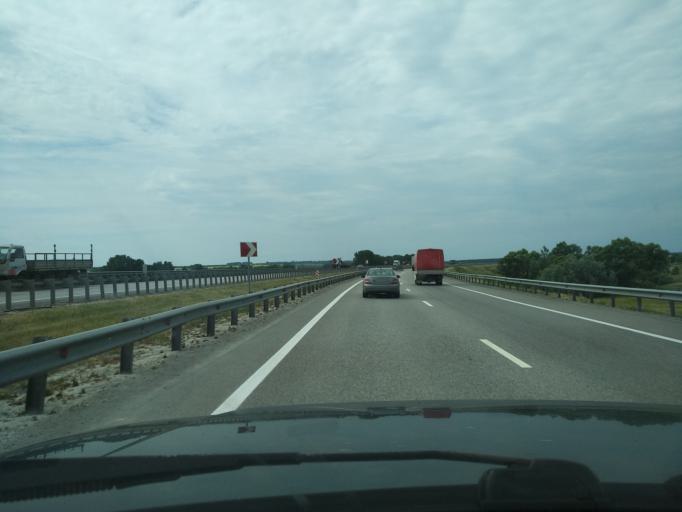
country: RU
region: Lipetsk
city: Khlevnoye
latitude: 52.0603
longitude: 39.1834
